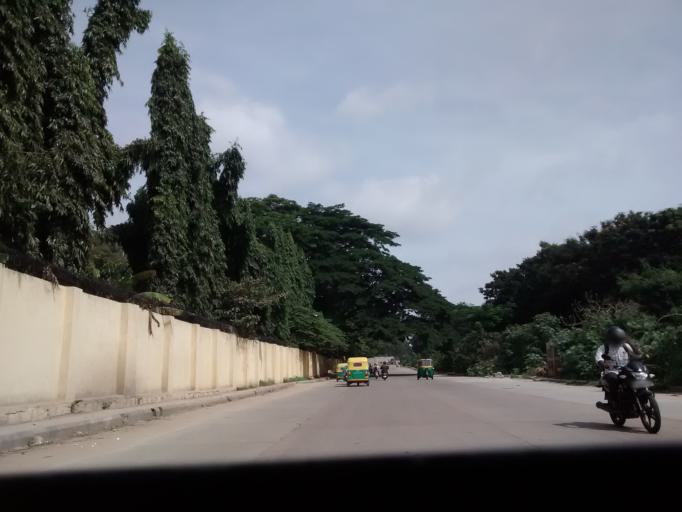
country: IN
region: Karnataka
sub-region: Bangalore Urban
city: Bangalore
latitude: 12.9775
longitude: 77.6541
